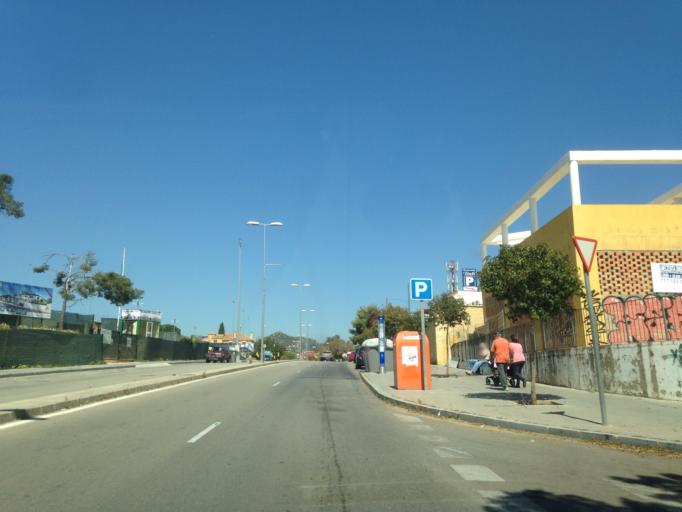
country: ES
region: Andalusia
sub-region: Provincia de Malaga
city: Malaga
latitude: 36.7415
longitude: -4.4877
